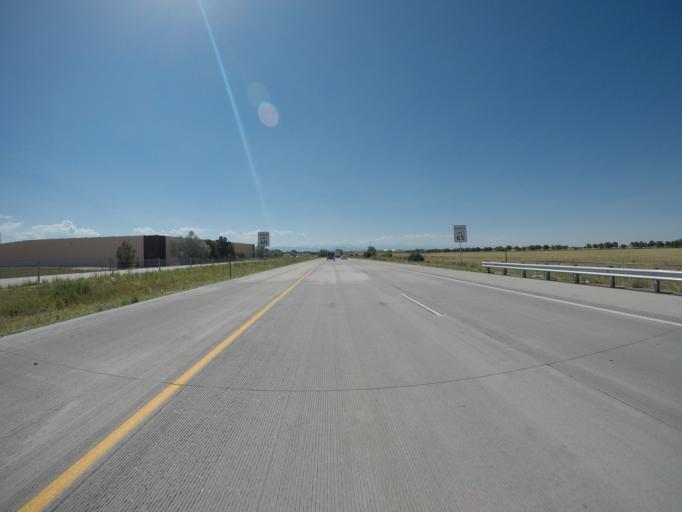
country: US
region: Colorado
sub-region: Adams County
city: Aurora
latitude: 39.7567
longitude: -104.7645
